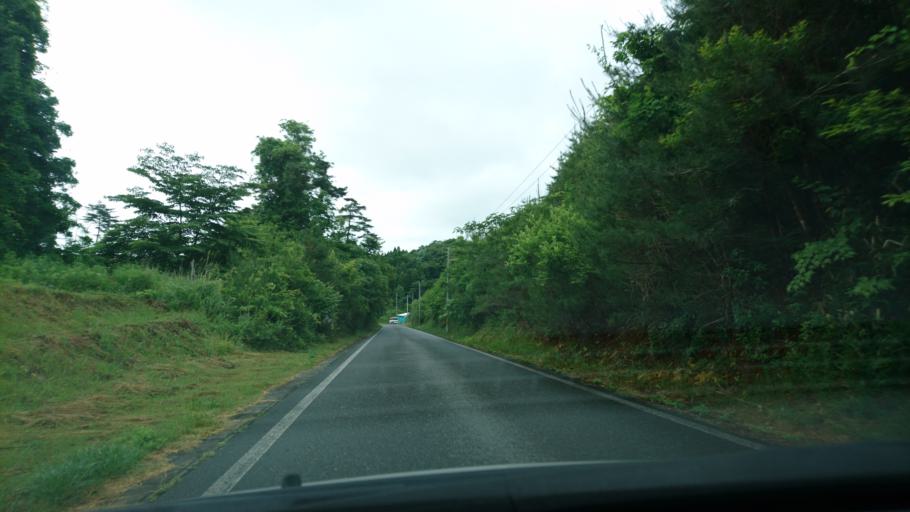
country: JP
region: Iwate
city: Ichinoseki
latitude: 38.8992
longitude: 141.1442
